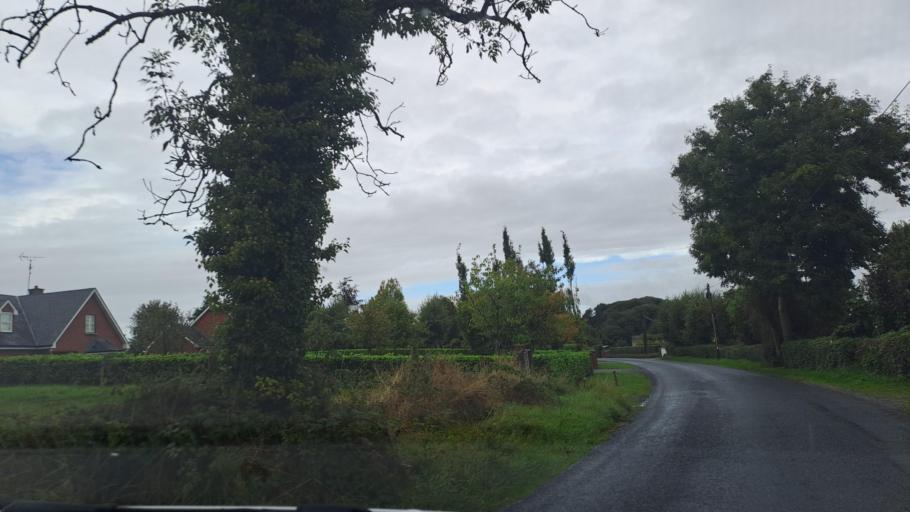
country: IE
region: Ulster
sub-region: County Monaghan
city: Carrickmacross
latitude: 53.9804
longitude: -6.7550
